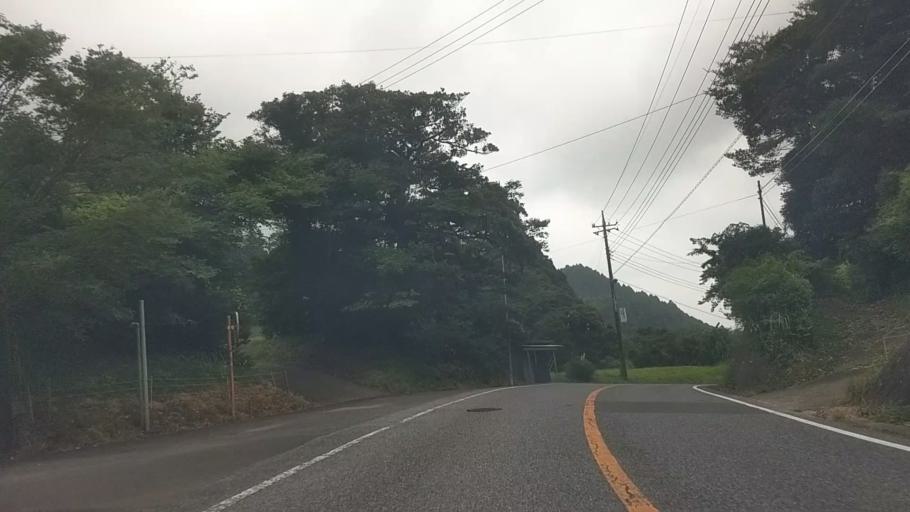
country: JP
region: Chiba
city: Tateyama
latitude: 35.1430
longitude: 139.9209
